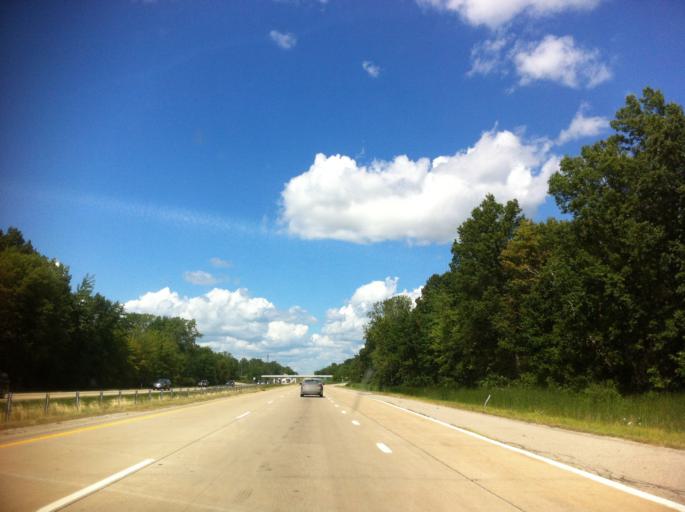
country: US
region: Michigan
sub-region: Monroe County
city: Dundee
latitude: 41.9048
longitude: -83.6617
